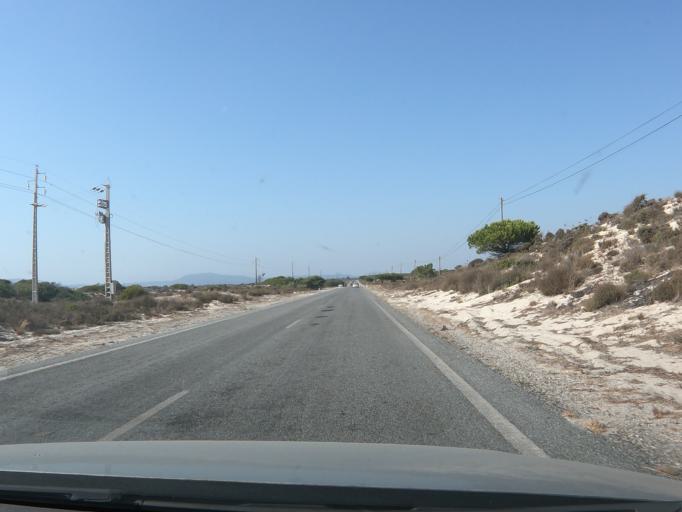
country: PT
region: Setubal
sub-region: Setubal
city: Setubal
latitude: 38.4241
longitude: -8.8228
